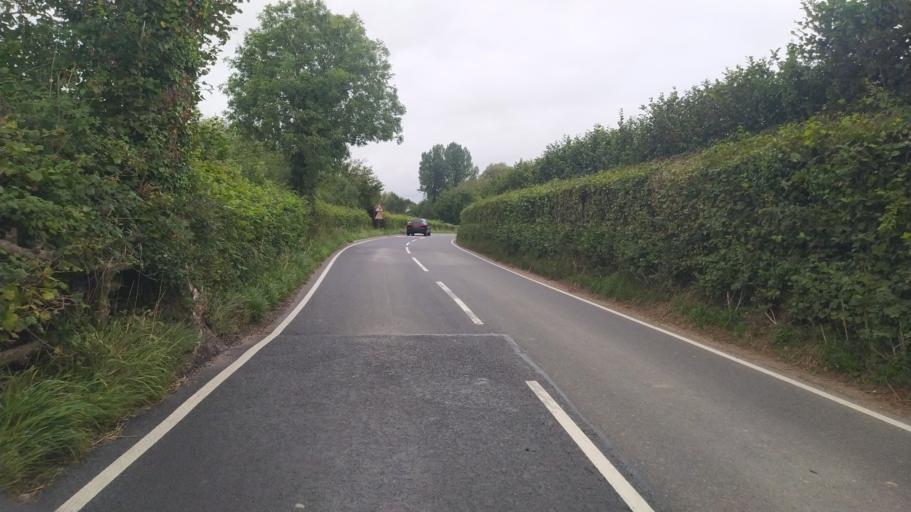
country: GB
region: England
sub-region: Dorset
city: Dorchester
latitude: 50.7556
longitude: -2.3606
